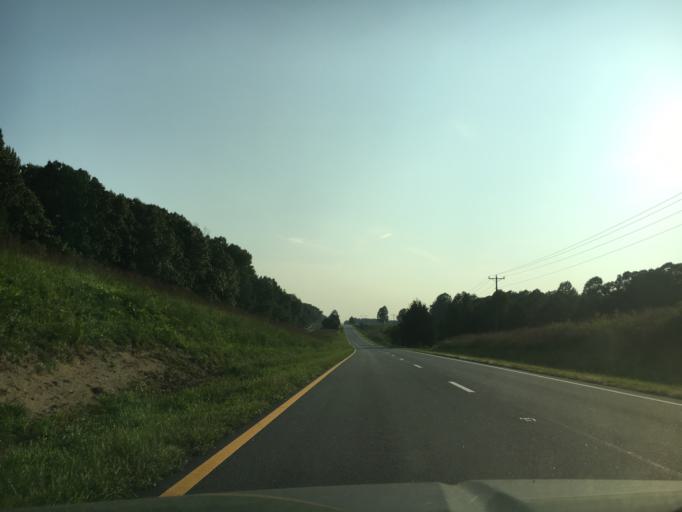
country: US
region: Virginia
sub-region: Prince Edward County
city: Hampden Sydney
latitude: 37.2832
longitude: -78.6199
